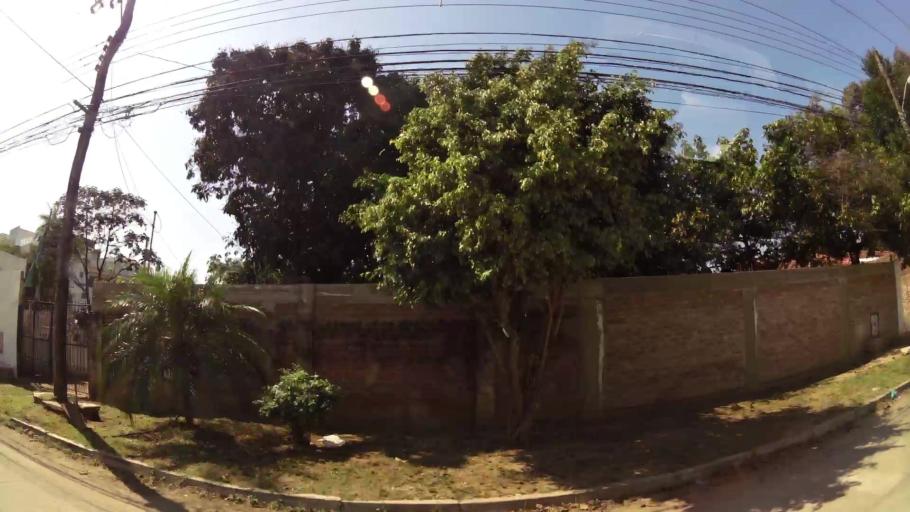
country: BO
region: Santa Cruz
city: Santa Cruz de la Sierra
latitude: -17.7488
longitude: -63.1729
